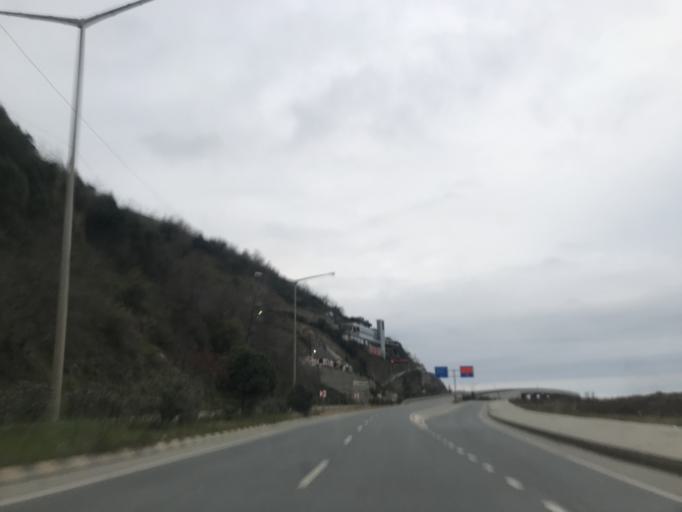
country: TR
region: Trabzon
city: Derecik
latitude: 40.9995
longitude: 39.6389
